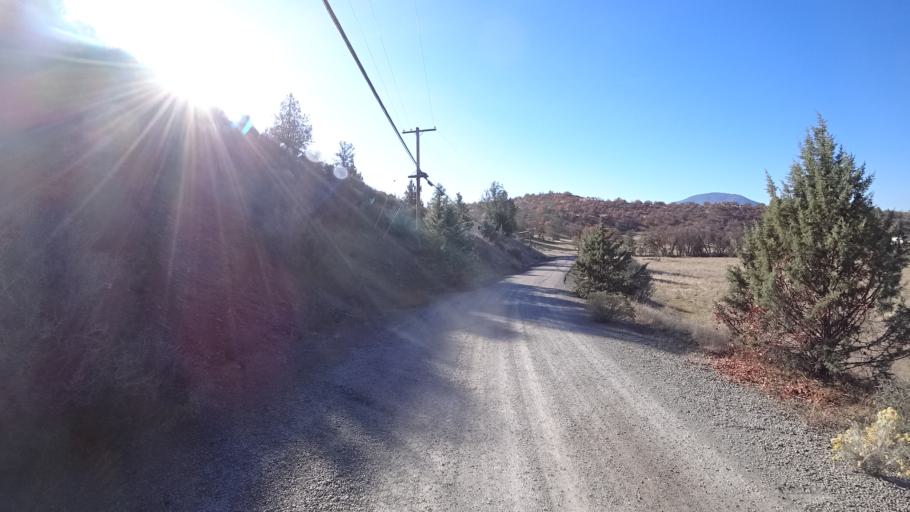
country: US
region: California
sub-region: Siskiyou County
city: Montague
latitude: 41.9194
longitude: -122.4485
